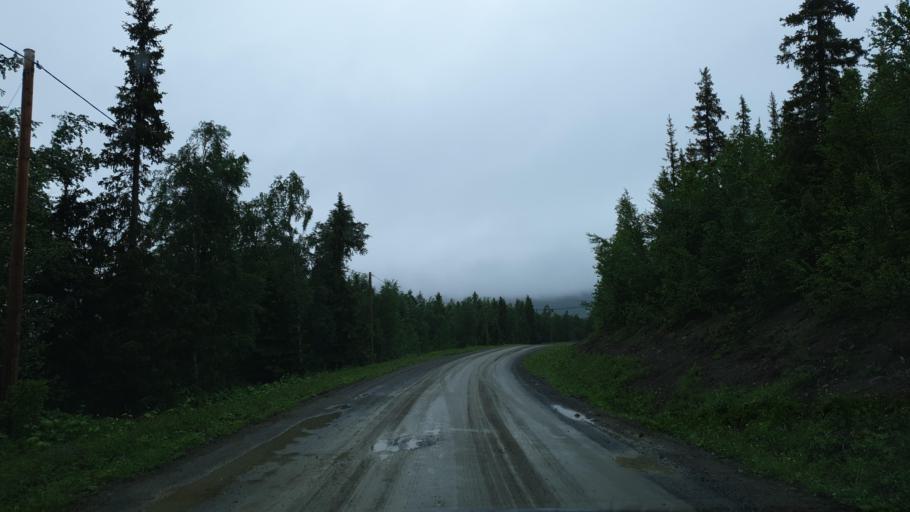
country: SE
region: Vaesterbotten
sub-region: Vilhelmina Kommun
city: Sjoberg
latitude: 65.3313
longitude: 15.8678
